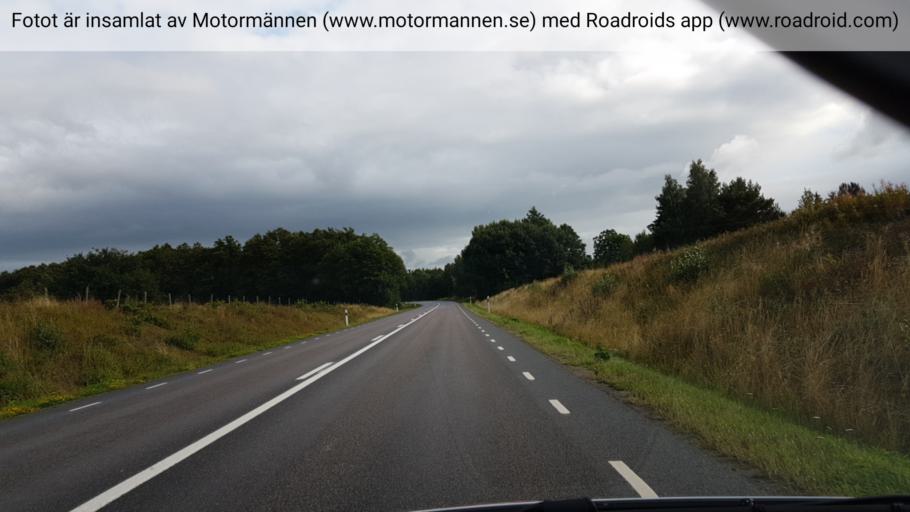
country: SE
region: Vaestra Goetaland
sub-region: Falkopings Kommun
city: Falkoeping
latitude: 58.2483
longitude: 13.5135
